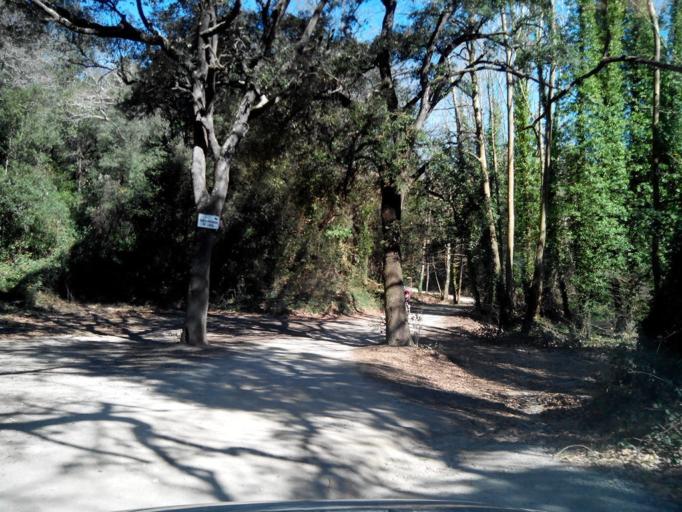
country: ES
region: Catalonia
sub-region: Provincia de Barcelona
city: Dosrius
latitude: 41.6025
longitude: 2.4523
